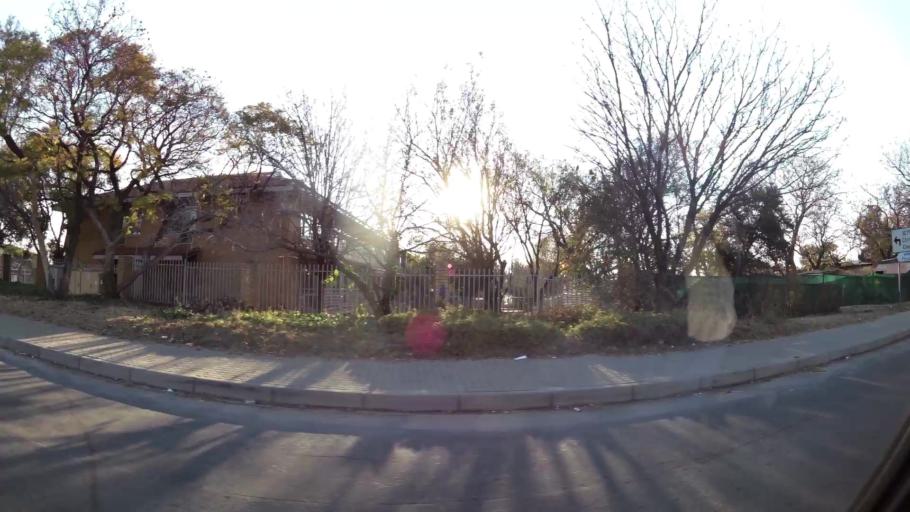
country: ZA
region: Gauteng
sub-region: City of Johannesburg Metropolitan Municipality
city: Midrand
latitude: -26.0063
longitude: 28.1167
